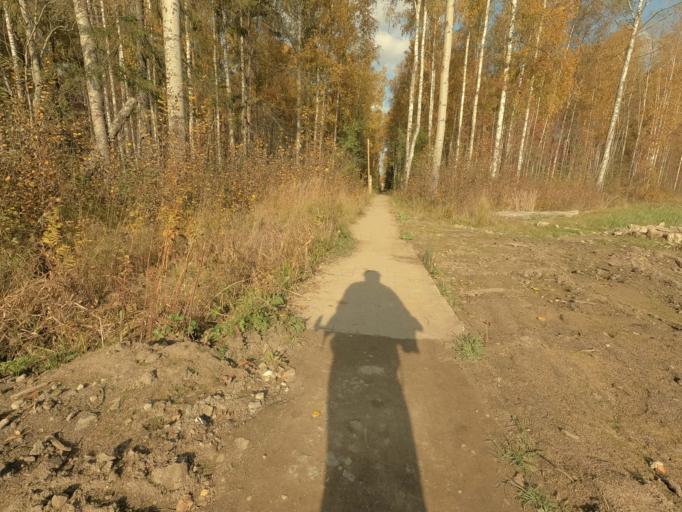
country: RU
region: Leningrad
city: Mga
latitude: 59.7602
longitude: 31.1143
